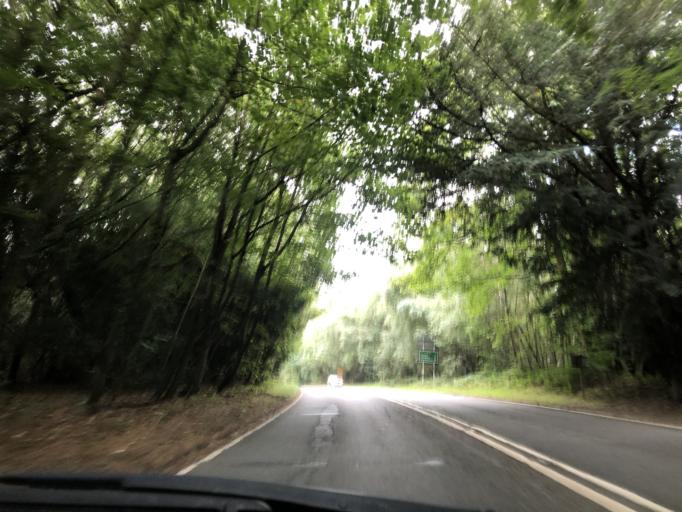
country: GB
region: England
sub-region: East Sussex
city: Forest Row
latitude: 51.0667
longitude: 0.0258
